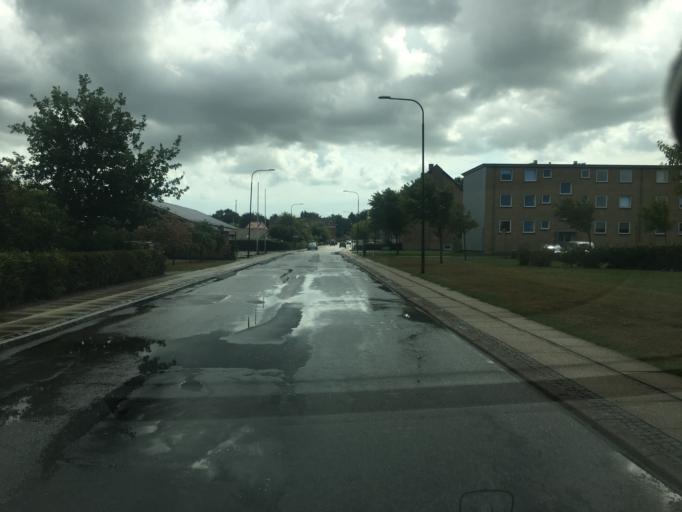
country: DK
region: South Denmark
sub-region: Tonder Kommune
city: Tonder
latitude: 54.9413
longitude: 8.8623
